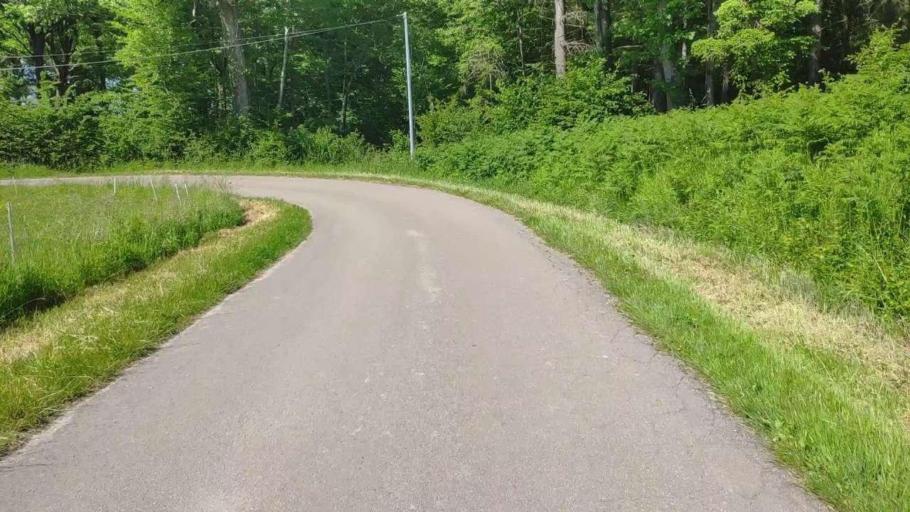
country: FR
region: Franche-Comte
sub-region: Departement du Jura
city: Bletterans
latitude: 46.8114
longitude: 5.4115
